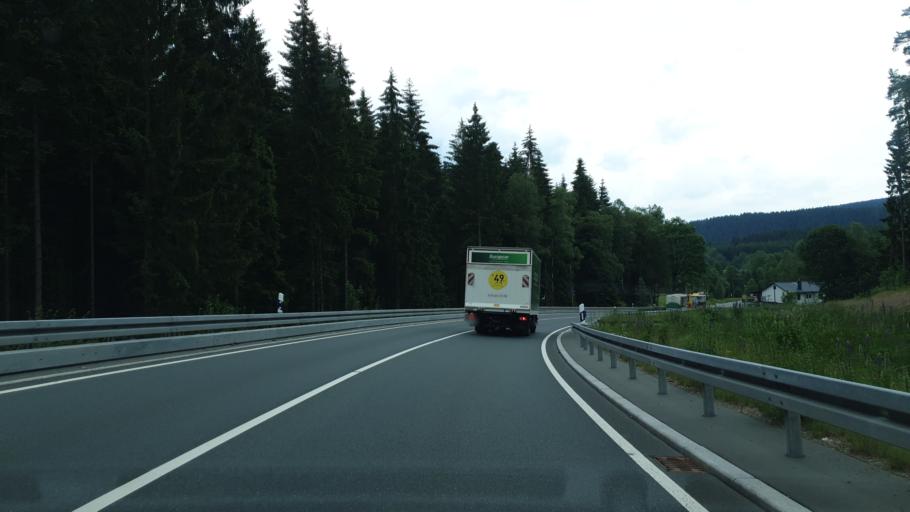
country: DE
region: Saxony
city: Tannenbergsthal
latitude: 50.4540
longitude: 12.4627
